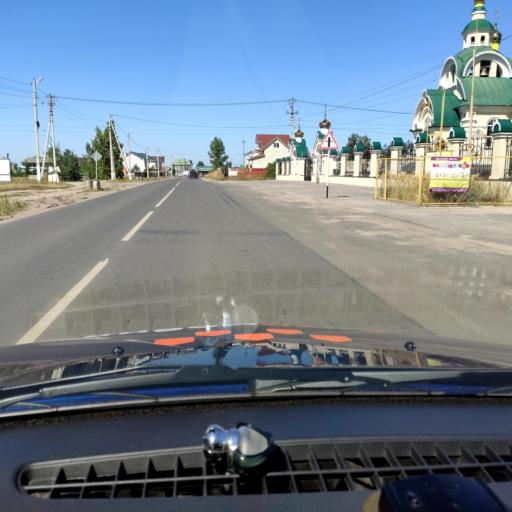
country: RU
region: Voronezj
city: Podgornoye
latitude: 51.7879
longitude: 39.1460
